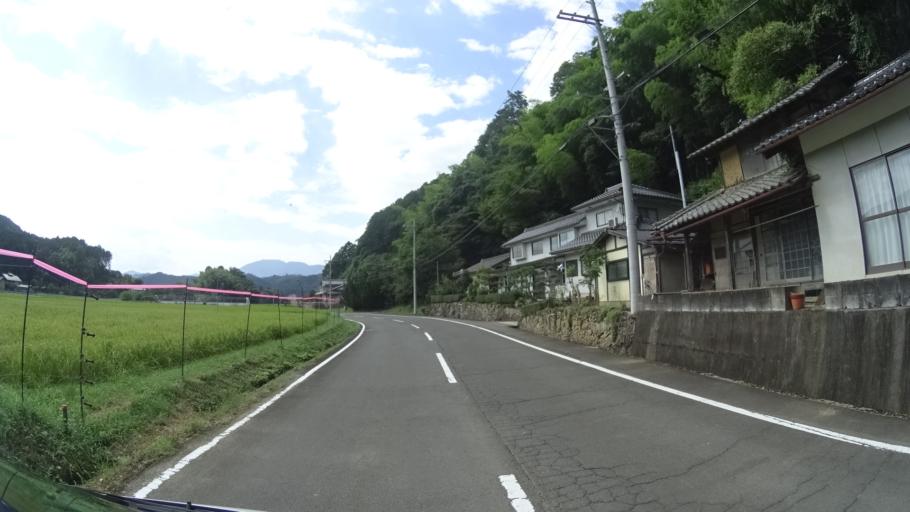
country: JP
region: Kyoto
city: Fukuchiyama
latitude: 35.3748
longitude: 135.1487
